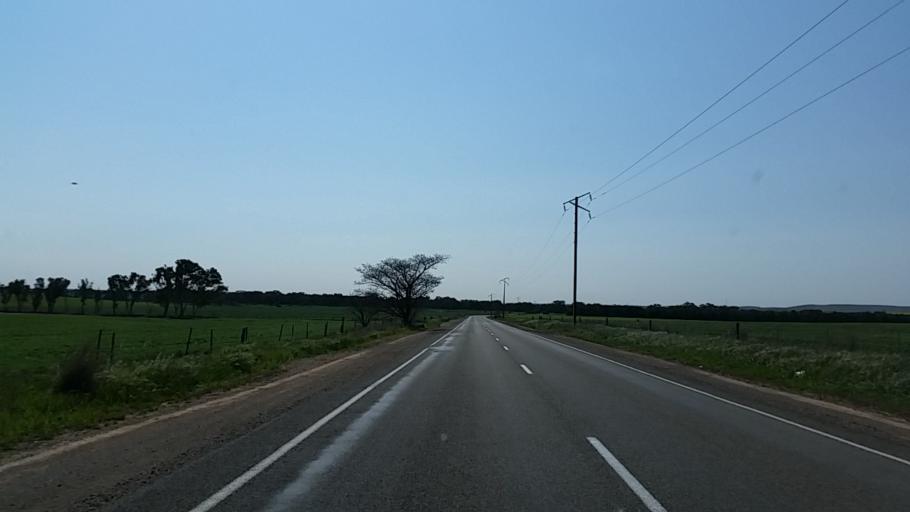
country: AU
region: South Australia
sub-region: Port Pirie City and Dists
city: Crystal Brook
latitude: -33.2687
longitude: 138.3216
